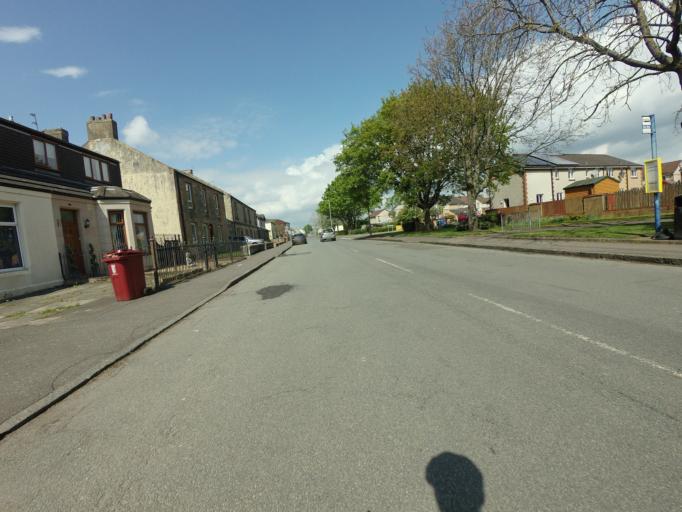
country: GB
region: Scotland
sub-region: Falkirk
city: Falkirk
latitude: 56.0279
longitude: -3.7816
